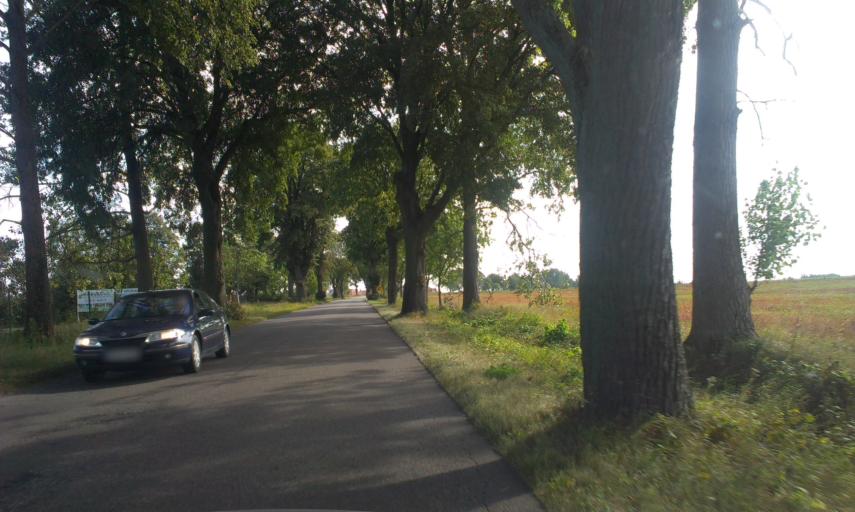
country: PL
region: Greater Poland Voivodeship
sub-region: Powiat zlotowski
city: Zlotow
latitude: 53.3904
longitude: 17.0072
